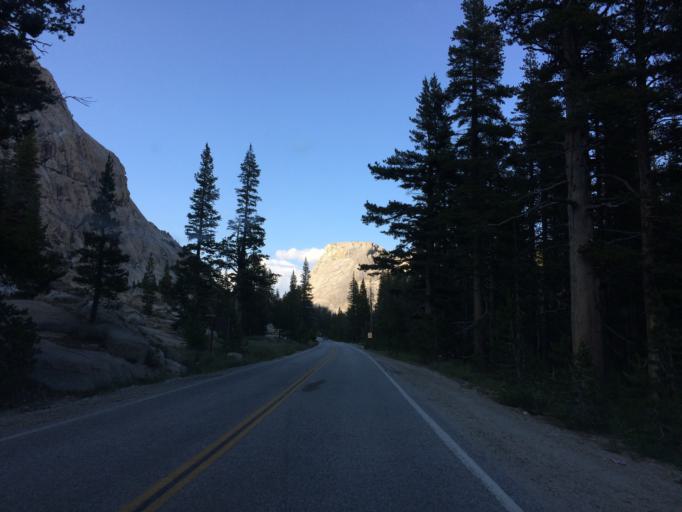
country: US
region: California
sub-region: Mariposa County
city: Yosemite Valley
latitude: 37.8384
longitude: -119.4519
